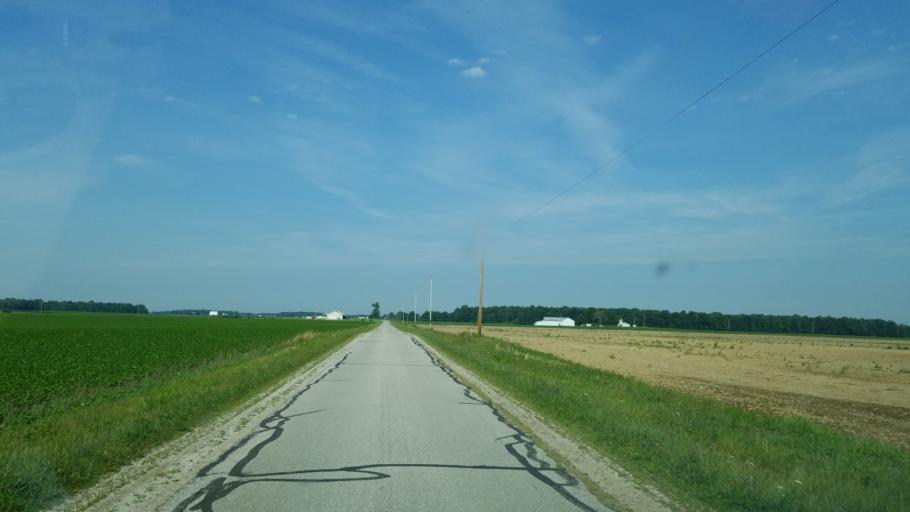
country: US
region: Ohio
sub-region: Huron County
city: Willard
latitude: 41.0374
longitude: -82.9132
